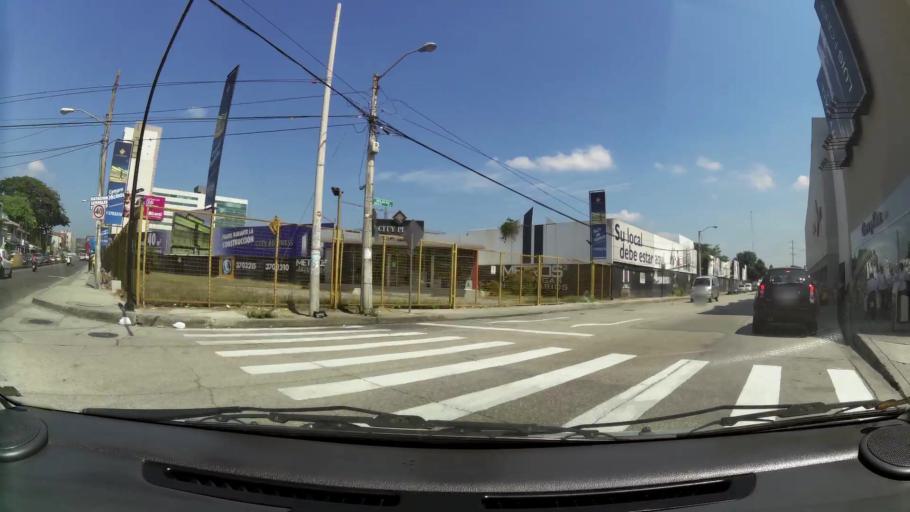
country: EC
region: Guayas
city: Eloy Alfaro
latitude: -2.1420
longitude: -79.9093
